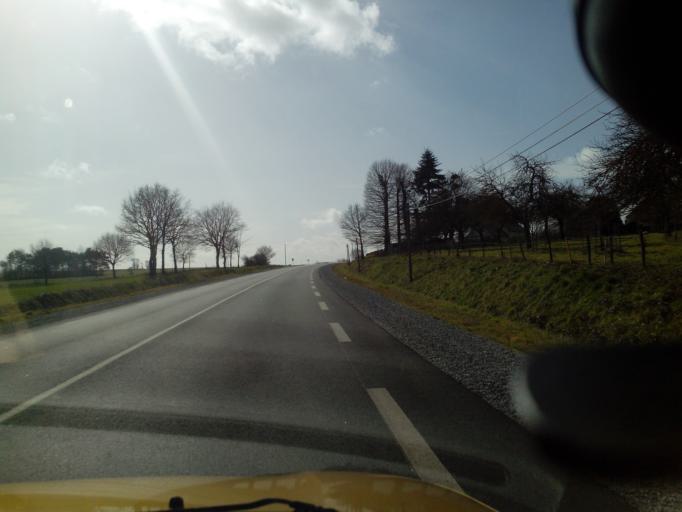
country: FR
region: Brittany
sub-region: Departement du Morbihan
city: Mauron
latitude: 48.0594
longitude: -2.2926
